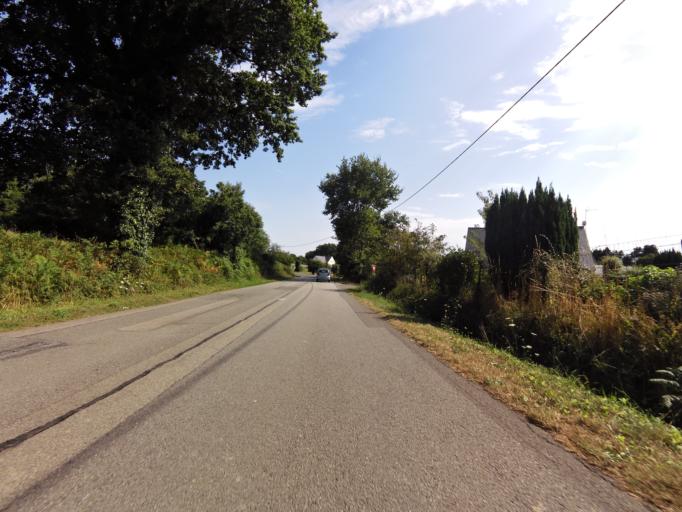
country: FR
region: Brittany
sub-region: Departement du Morbihan
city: Limerzel
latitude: 47.6412
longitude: -2.3604
